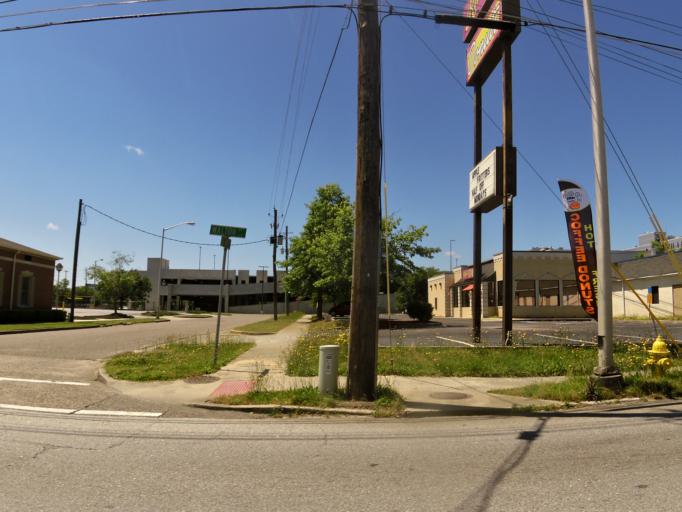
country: US
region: Georgia
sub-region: Richmond County
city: Augusta
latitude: 33.4745
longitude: -81.9853
